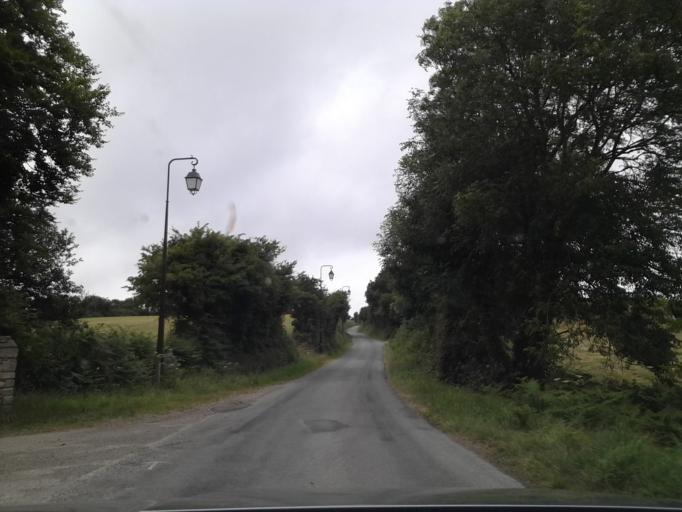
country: FR
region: Lower Normandy
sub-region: Departement de la Manche
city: Beaumont-Hague
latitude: 49.6842
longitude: -1.8648
